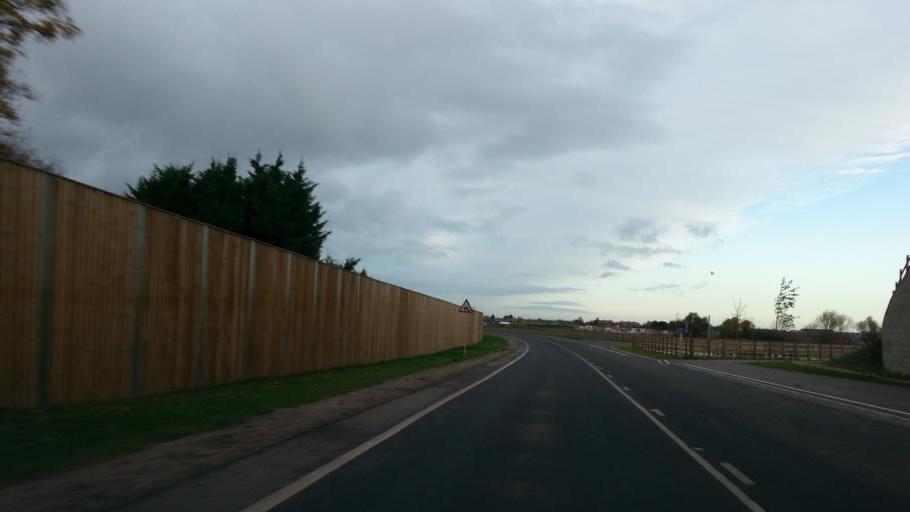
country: GB
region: England
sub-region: Nottinghamshire
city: Newark on Trent
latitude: 53.0507
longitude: -0.8002
